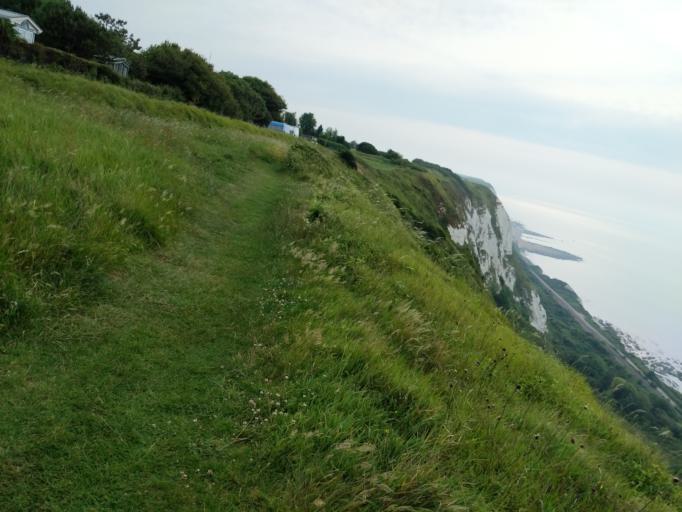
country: GB
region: England
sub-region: Kent
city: Folkestone
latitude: 51.1012
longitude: 1.2203
